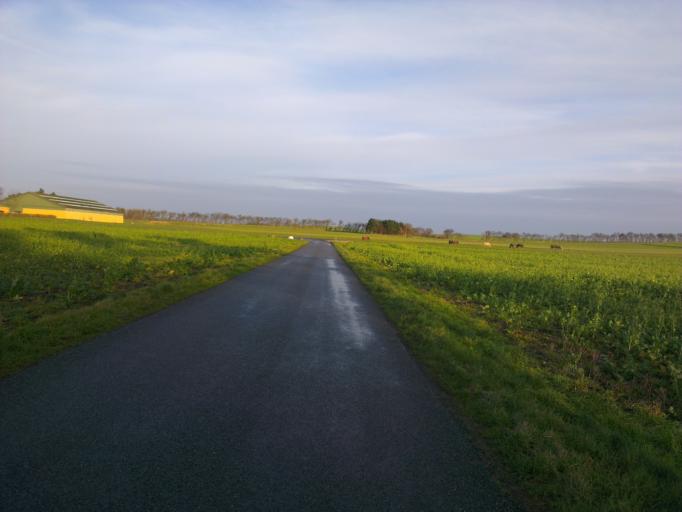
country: DK
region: Capital Region
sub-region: Frederikssund Kommune
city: Jaegerspris
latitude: 55.8387
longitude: 11.9713
